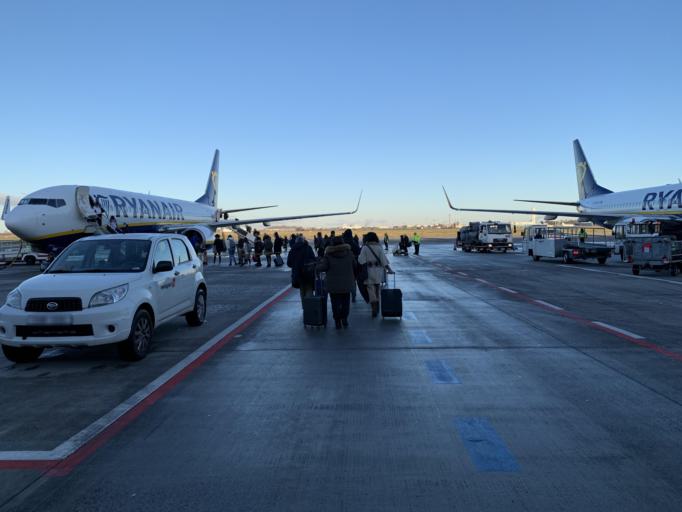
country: DE
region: Brandenburg
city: Schonefeld
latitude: 52.3678
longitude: 13.5091
